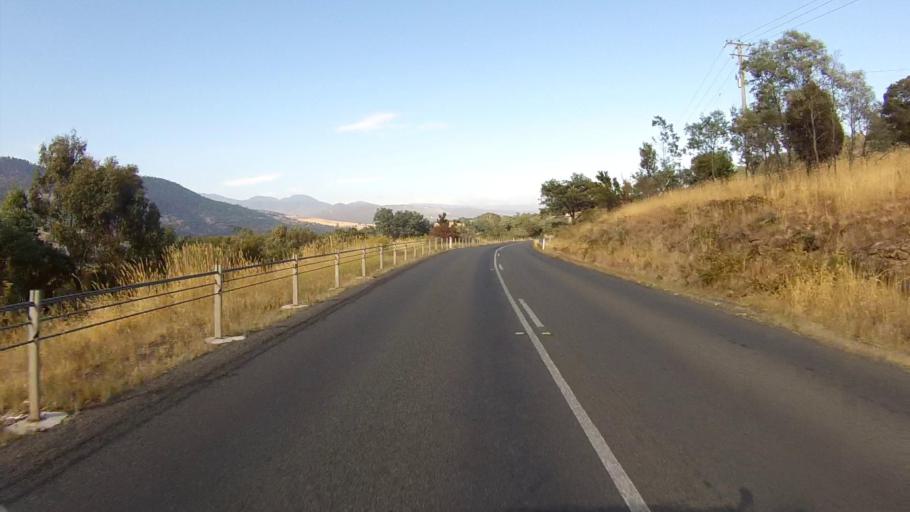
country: AU
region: Tasmania
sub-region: Glenorchy
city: Granton
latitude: -42.7539
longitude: 147.1465
